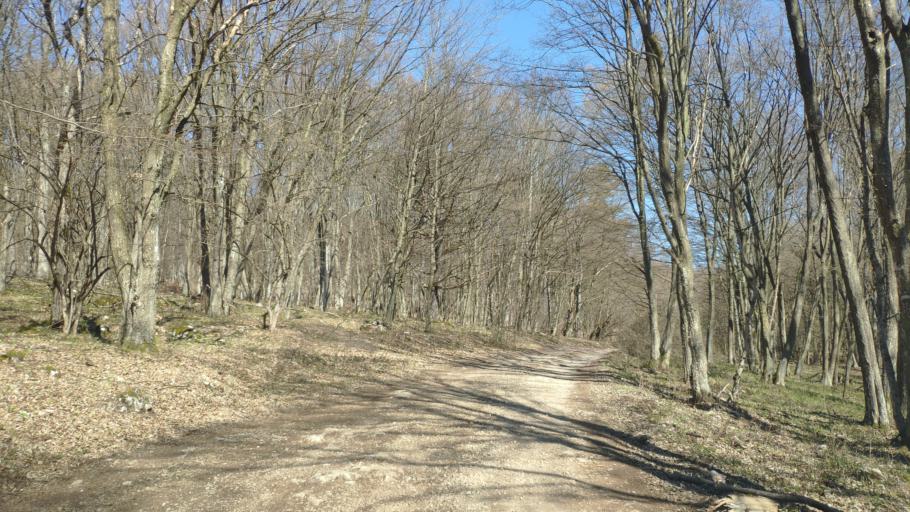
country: SK
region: Kosicky
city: Roznava
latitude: 48.6002
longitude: 20.4106
